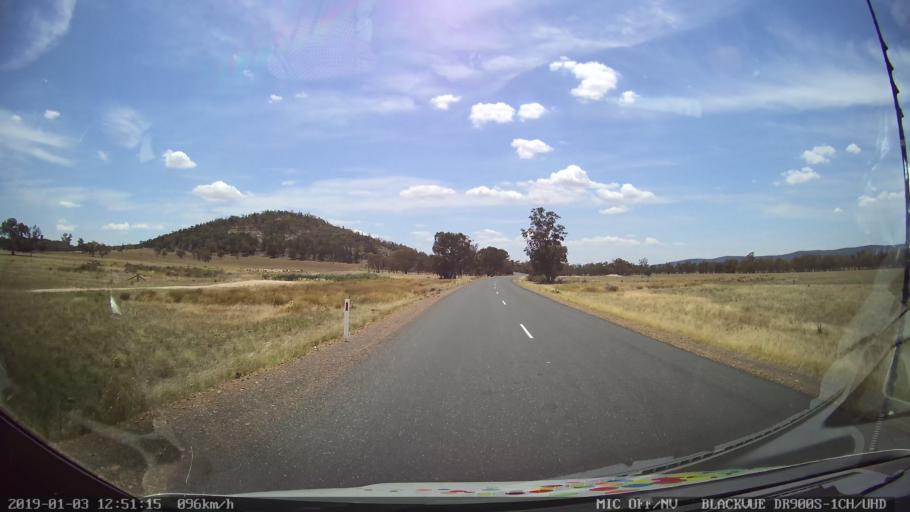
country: AU
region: New South Wales
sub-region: Weddin
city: Grenfell
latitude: -33.6815
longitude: 148.2784
